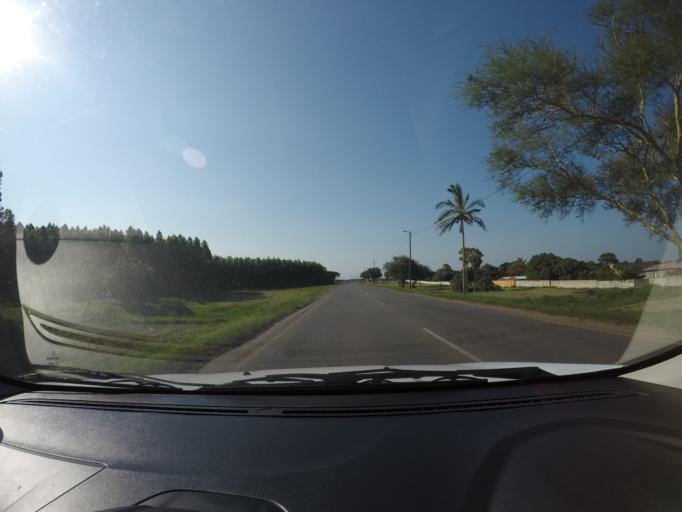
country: ZA
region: KwaZulu-Natal
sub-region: uThungulu District Municipality
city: Richards Bay
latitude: -28.7177
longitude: 32.0318
